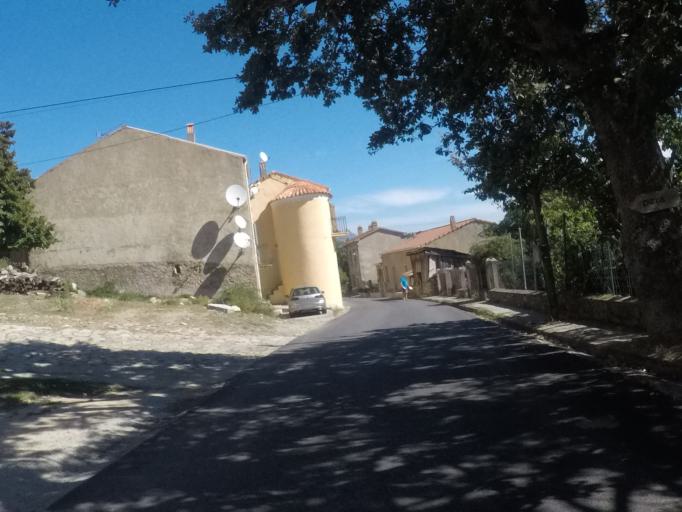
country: FR
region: Corsica
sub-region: Departement de la Haute-Corse
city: Corte
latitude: 42.3184
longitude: 9.0026
